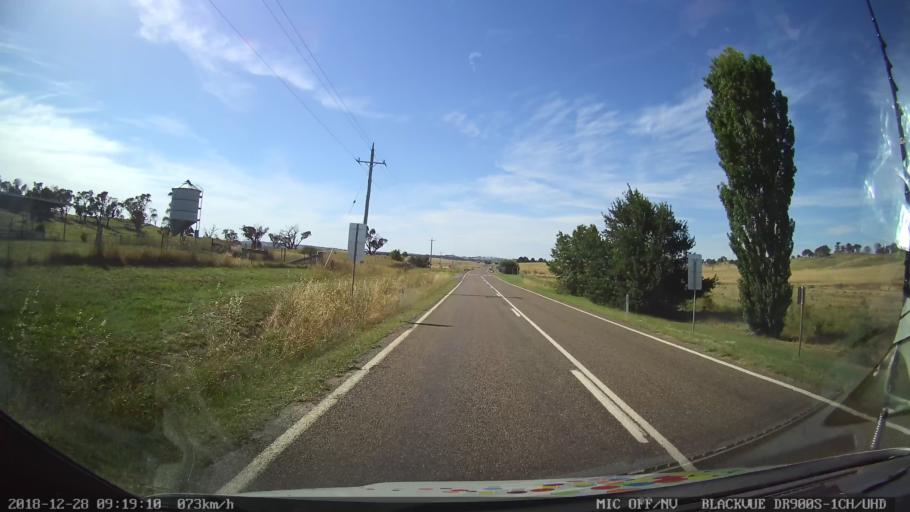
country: AU
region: New South Wales
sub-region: Upper Lachlan Shire
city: Crookwell
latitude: -34.3335
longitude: 149.3674
